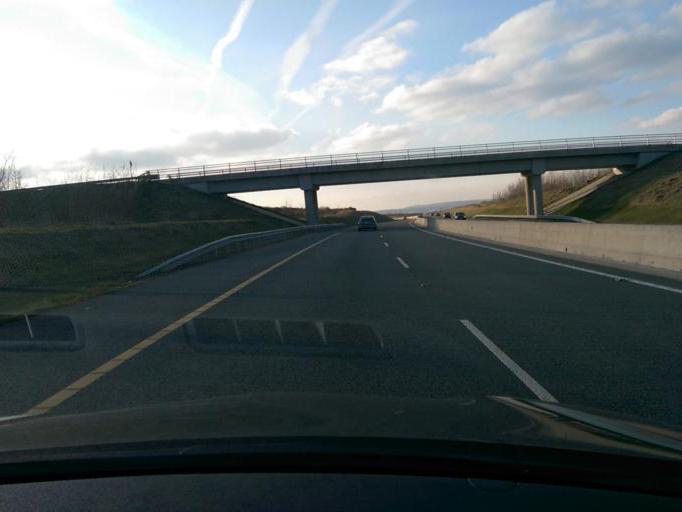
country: IE
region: Leinster
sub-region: Laois
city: Rathdowney
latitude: 52.9220
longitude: -7.5810
